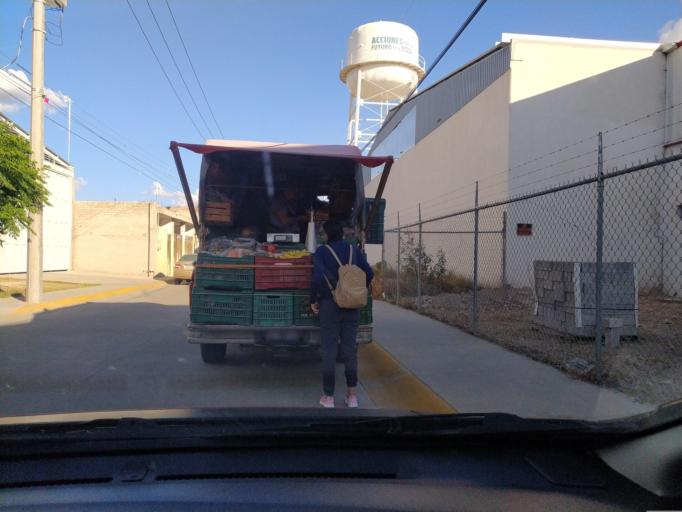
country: MX
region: Guanajuato
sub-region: San Francisco del Rincon
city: Estacion de San Francisco
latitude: 21.0268
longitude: -101.8266
